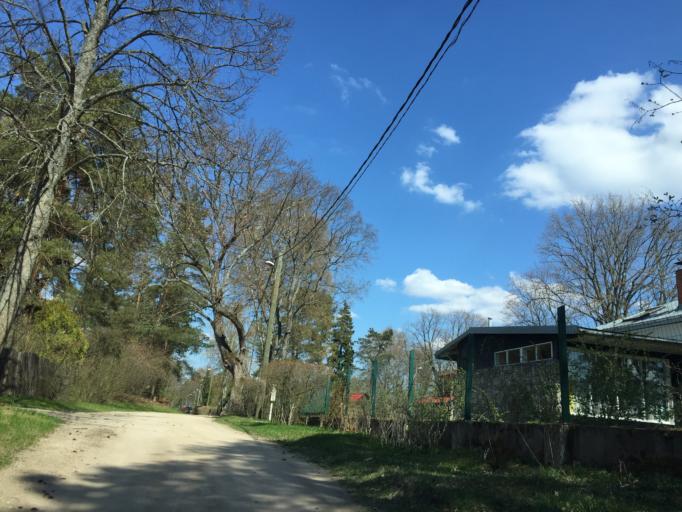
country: LV
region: Saulkrastu
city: Saulkrasti
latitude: 57.2310
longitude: 24.3901
